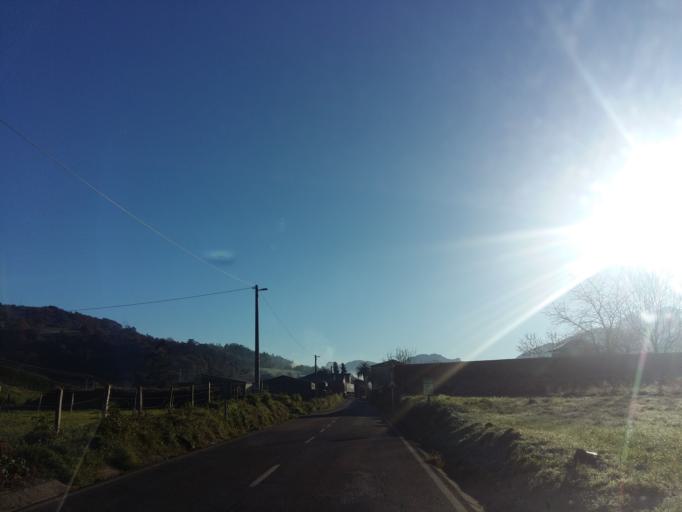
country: ES
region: Cantabria
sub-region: Provincia de Cantabria
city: Ramales de la Victoria
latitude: 43.2798
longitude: -3.5302
